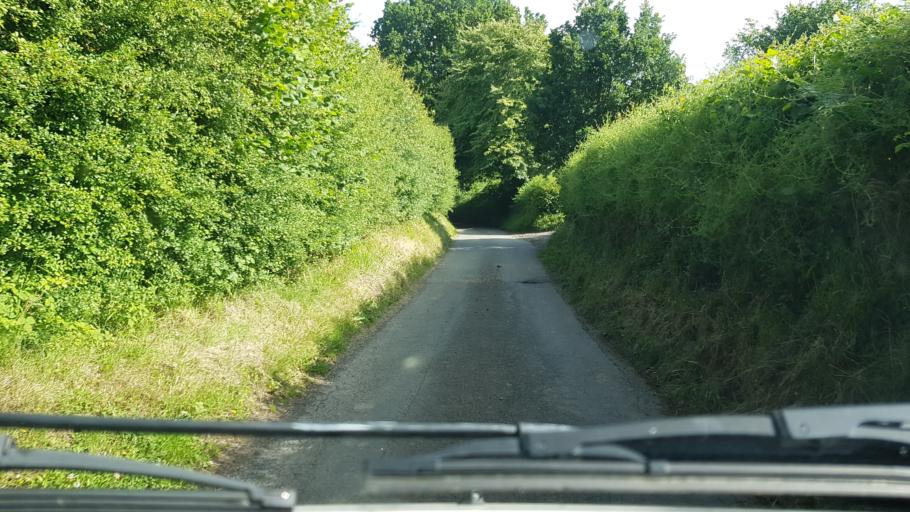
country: GB
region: England
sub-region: Worcestershire
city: Bewdley
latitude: 52.3498
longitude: -2.3311
